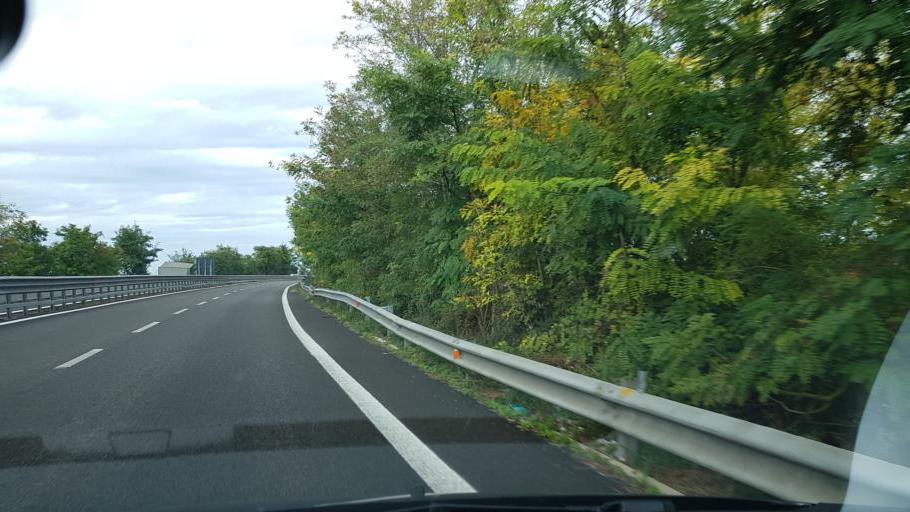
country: IT
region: Apulia
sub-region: Provincia di Lecce
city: Castromediano
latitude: 40.3266
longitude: 18.1855
